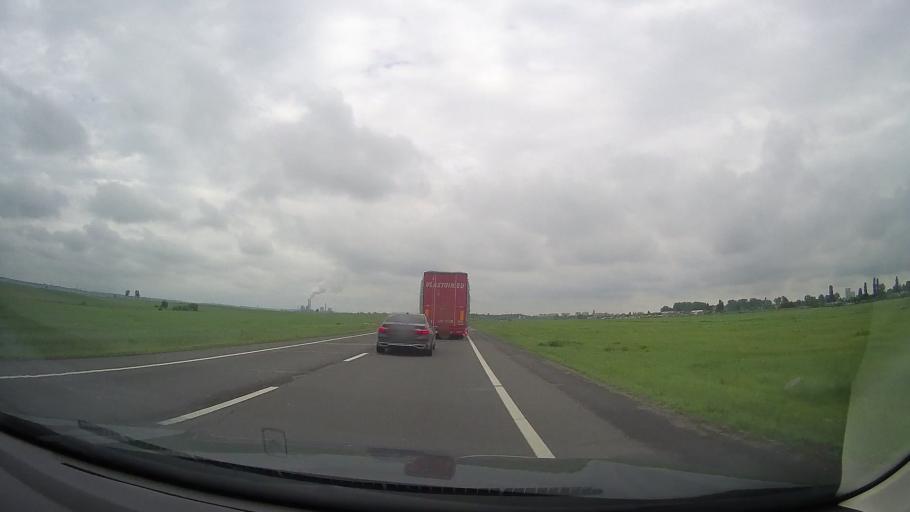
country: RO
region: Dolj
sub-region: Municipiul Craiova
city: Cernele
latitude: 44.3632
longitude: 23.7586
